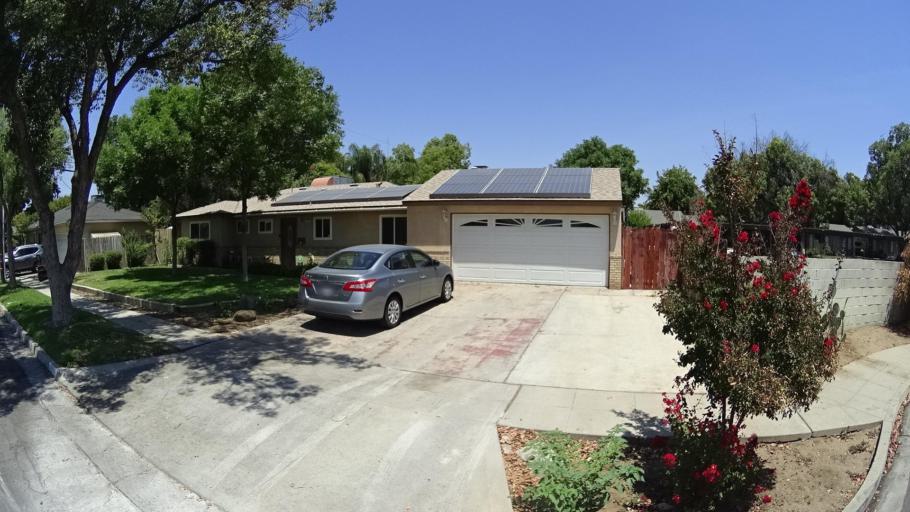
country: US
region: California
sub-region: Fresno County
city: Fresno
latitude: 36.7950
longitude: -119.7653
